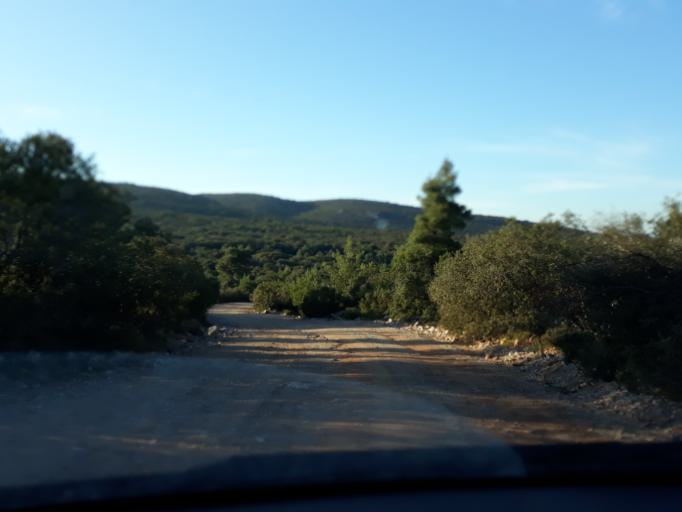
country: GR
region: Central Greece
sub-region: Nomos Voiotias
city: Ayios Thomas
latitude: 38.2358
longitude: 23.5340
